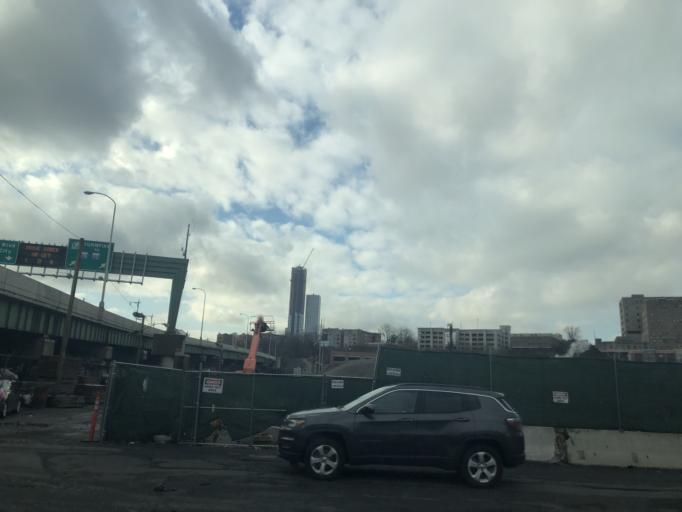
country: US
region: New Jersey
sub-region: Hudson County
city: Hoboken
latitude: 40.7322
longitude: -74.0460
